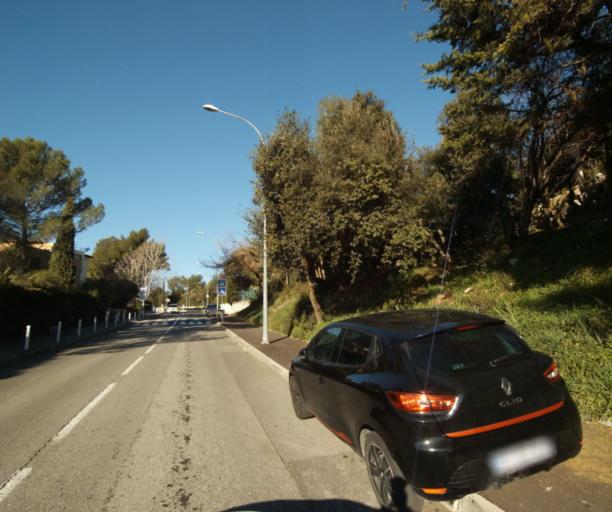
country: FR
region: Provence-Alpes-Cote d'Azur
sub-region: Departement des Alpes-Maritimes
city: Vallauris
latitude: 43.5973
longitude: 7.0717
